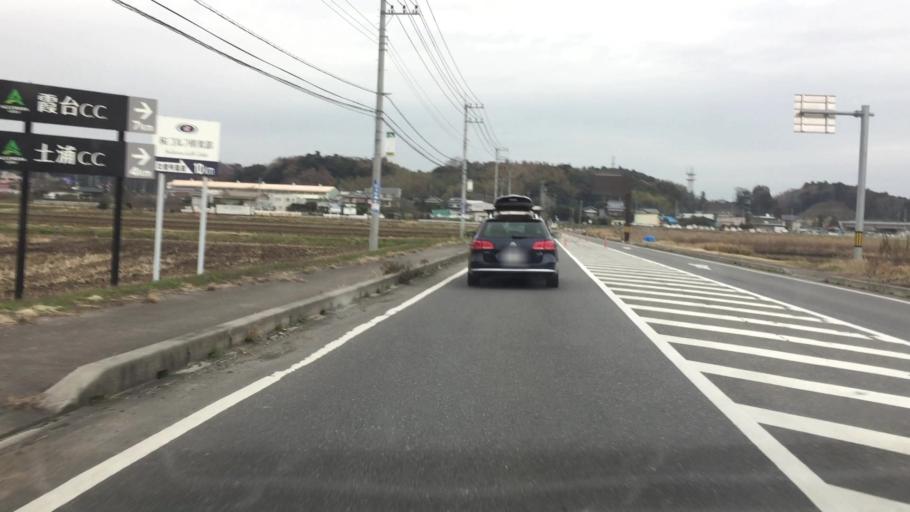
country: JP
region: Ibaraki
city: Edosaki
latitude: 35.9239
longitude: 140.3441
